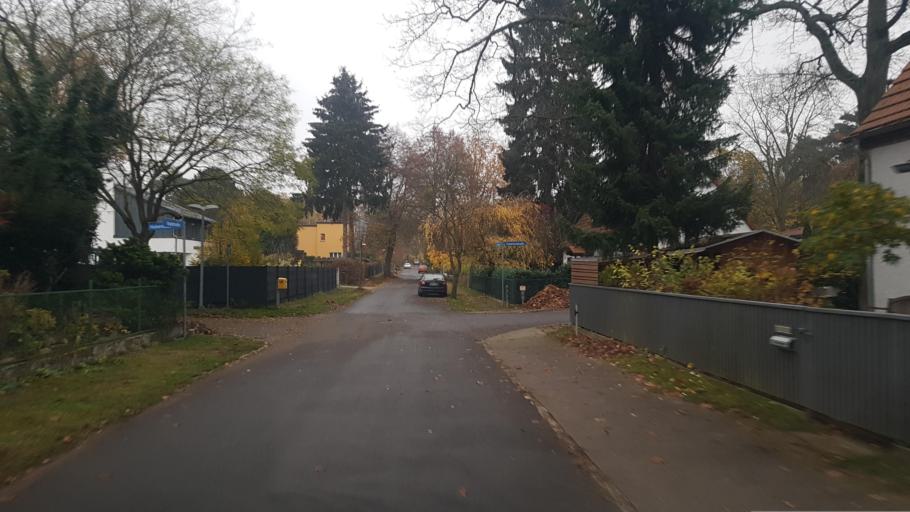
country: DE
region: Brandenburg
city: Michendorf
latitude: 52.3205
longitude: 13.0295
